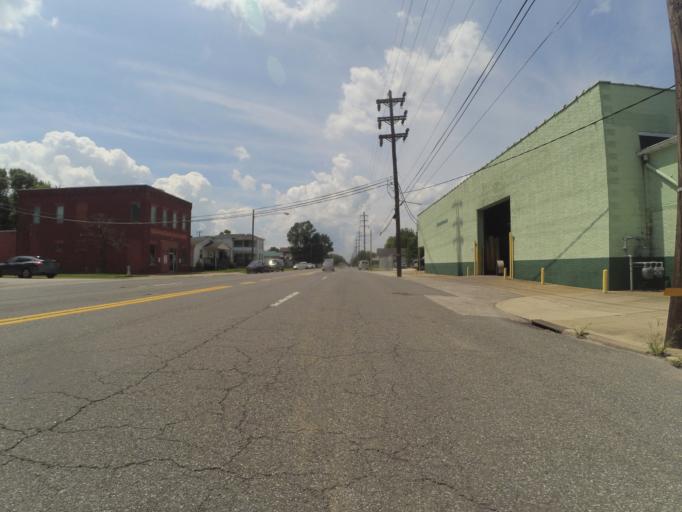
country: US
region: West Virginia
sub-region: Cabell County
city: Huntington
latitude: 38.4185
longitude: -82.4229
